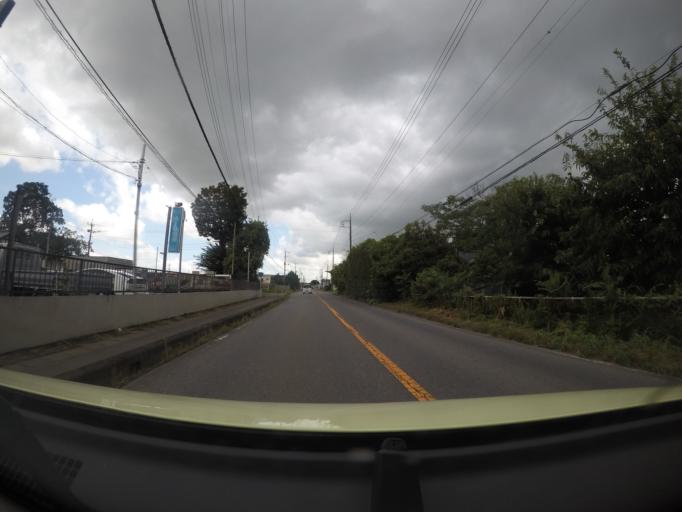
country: JP
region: Ibaraki
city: Iwai
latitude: 36.0367
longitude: 139.9373
